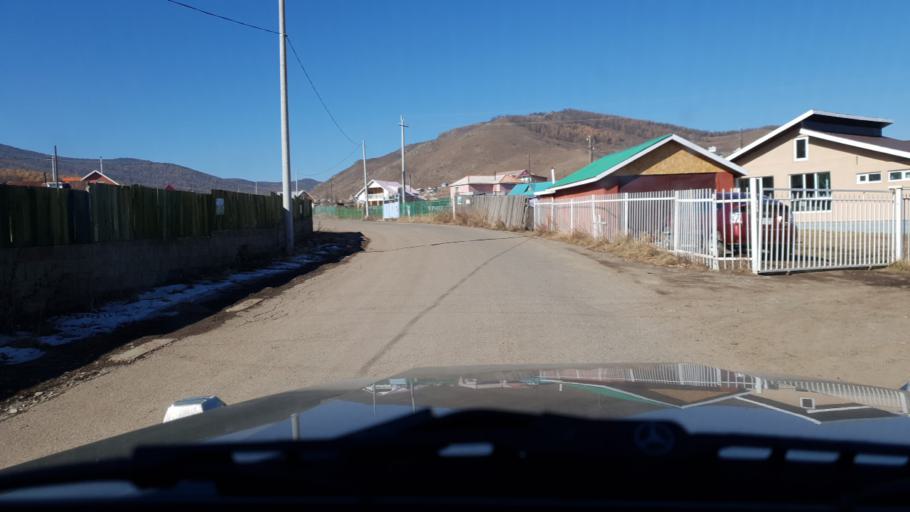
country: MN
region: Ulaanbaatar
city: Ulaanbaatar
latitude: 48.0505
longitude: 106.8977
